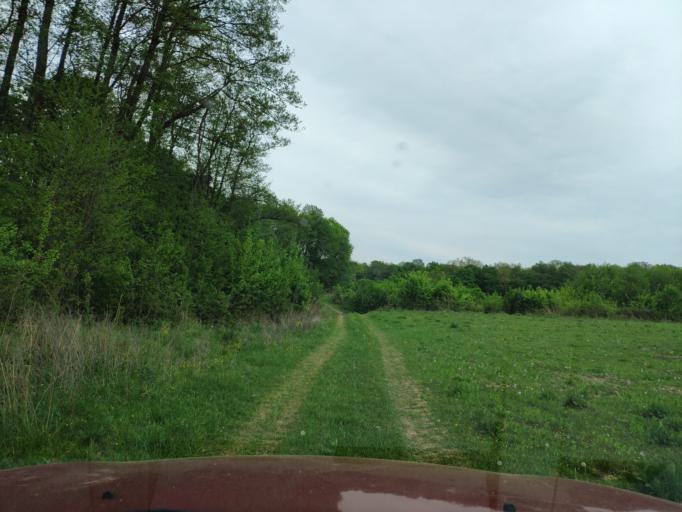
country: SK
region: Banskobystricky
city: Revuca
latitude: 48.5191
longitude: 20.1471
